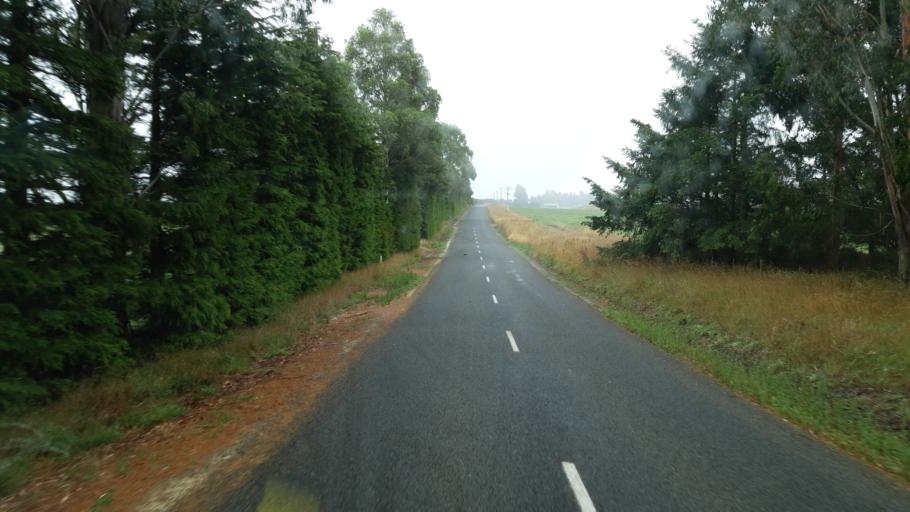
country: NZ
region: Otago
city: Oamaru
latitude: -44.9393
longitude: 170.7306
